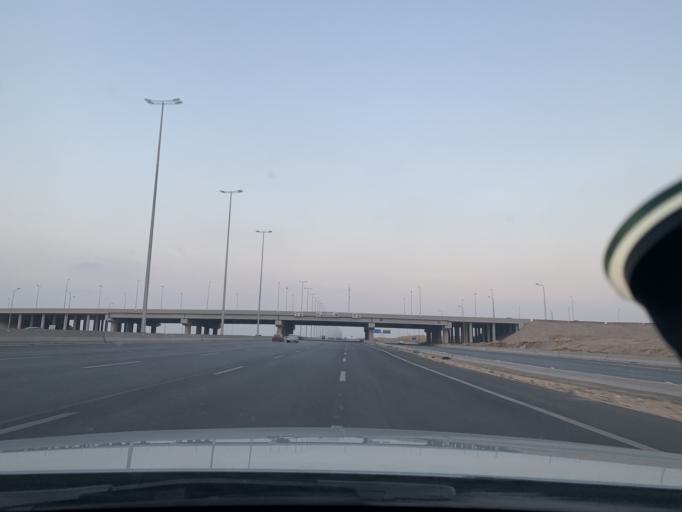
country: EG
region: Muhafazat al Qalyubiyah
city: Al Khankah
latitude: 30.0909
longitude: 31.5041
